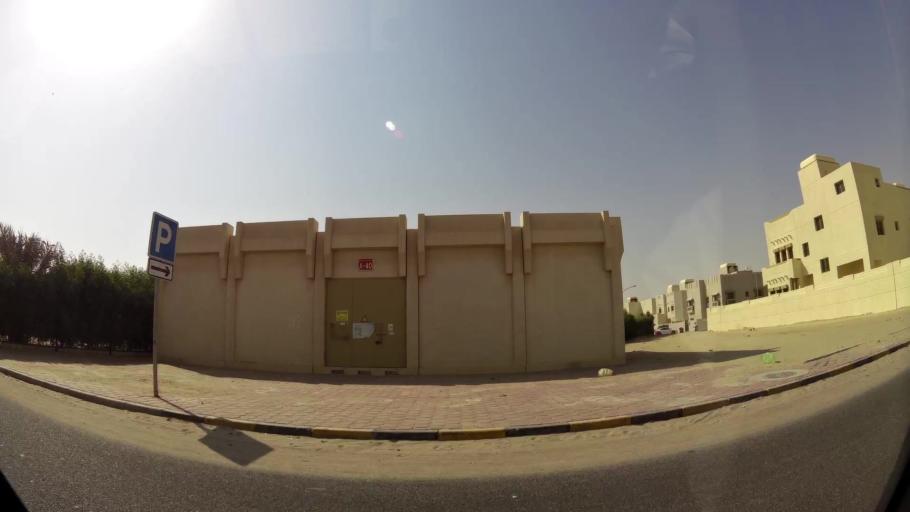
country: KW
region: Al Ahmadi
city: Al Wafrah
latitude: 28.8063
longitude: 48.0622
